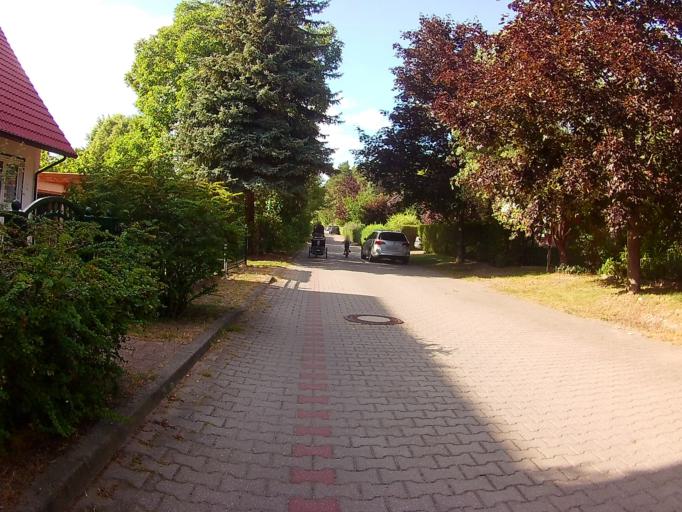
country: DE
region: Brandenburg
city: Schulzendorf
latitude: 52.3823
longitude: 13.5918
